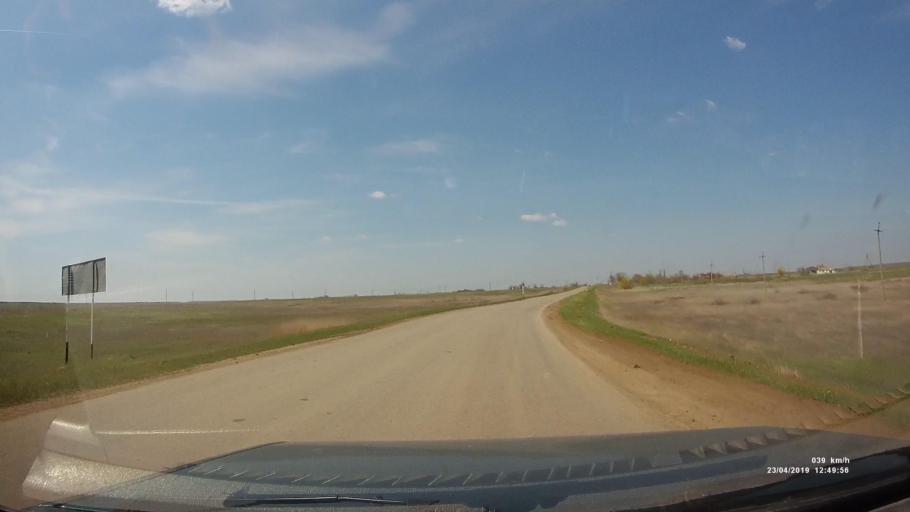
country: RU
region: Kalmykiya
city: Yashalta
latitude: 46.5419
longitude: 42.6402
